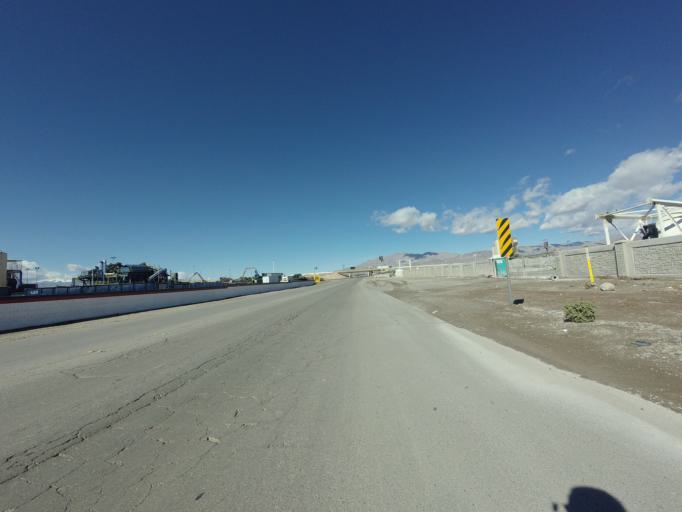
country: US
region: Nevada
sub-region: Clark County
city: Nellis Air Force Base
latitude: 36.2667
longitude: -115.0577
